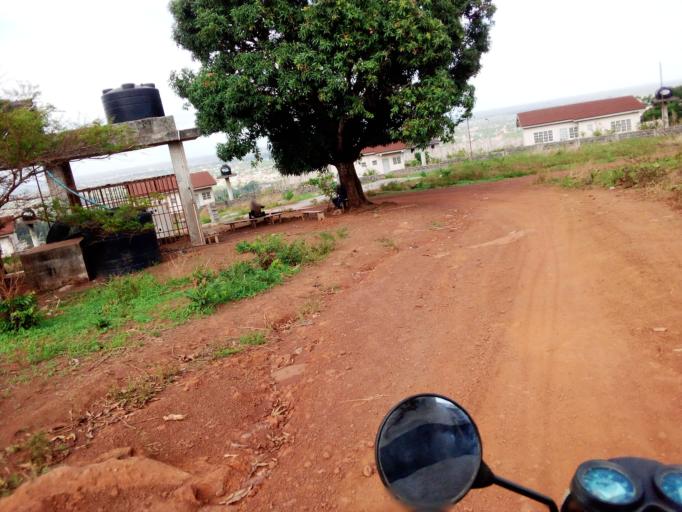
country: SL
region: Western Area
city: Waterloo
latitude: 8.3359
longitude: -13.0792
